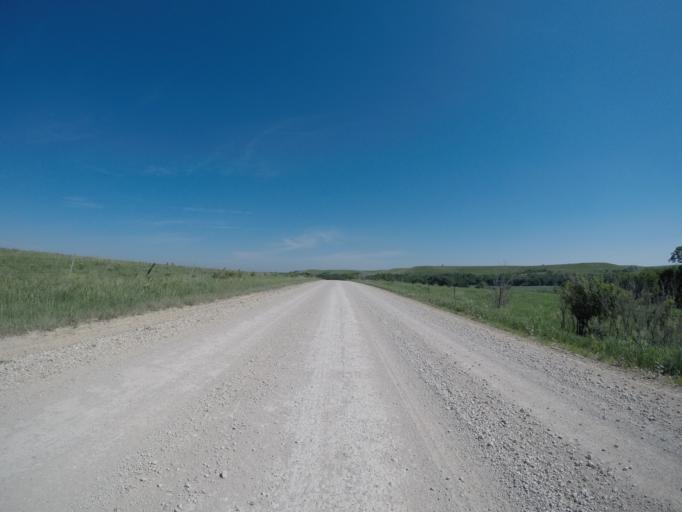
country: US
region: Kansas
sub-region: Wabaunsee County
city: Alma
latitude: 39.0171
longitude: -96.1413
